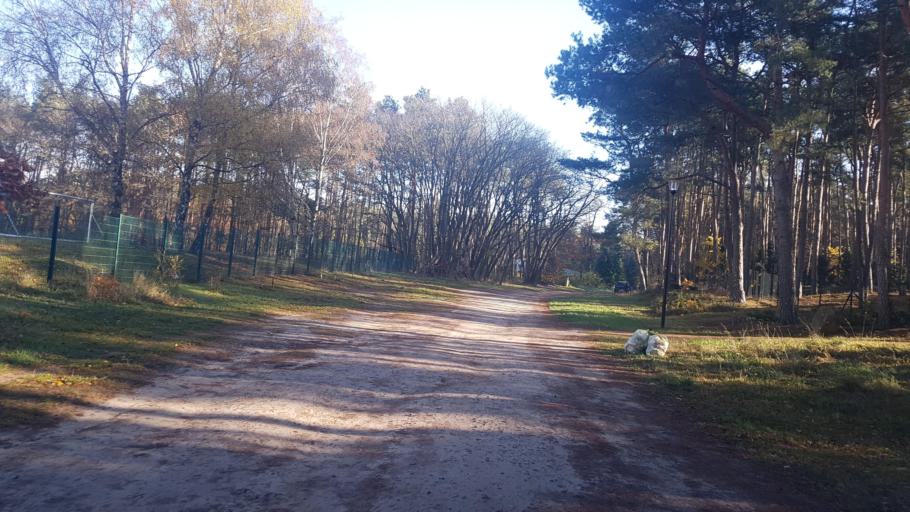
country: DE
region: Brandenburg
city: Niemegk
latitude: 52.0709
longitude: 12.7022
